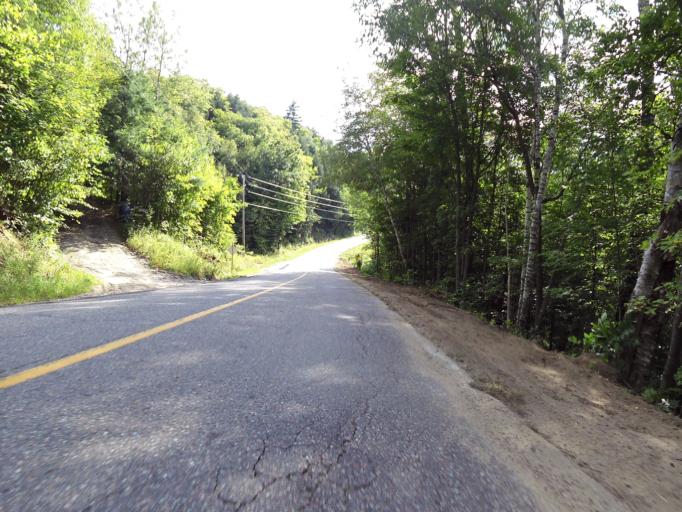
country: CA
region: Quebec
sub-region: Outaouais
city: Wakefield
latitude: 45.6807
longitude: -76.0034
